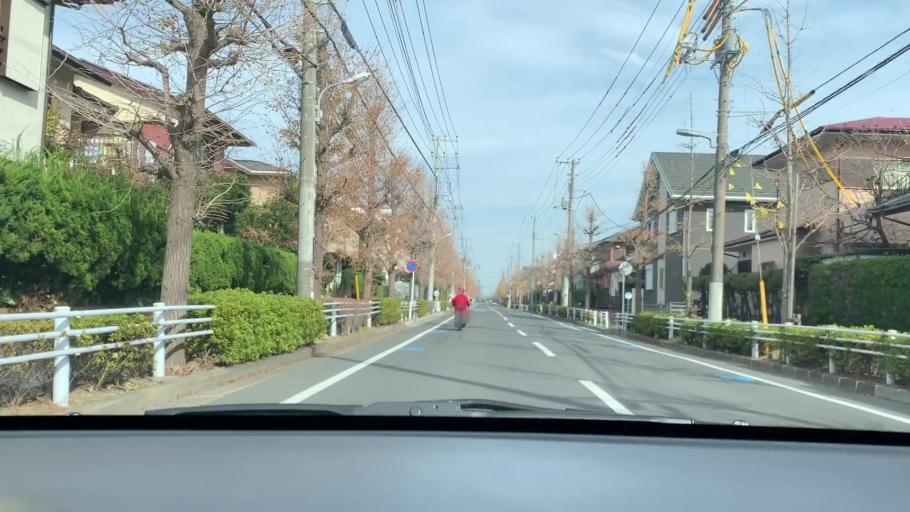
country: JP
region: Tokyo
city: Urayasu
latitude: 35.6407
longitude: 139.8964
